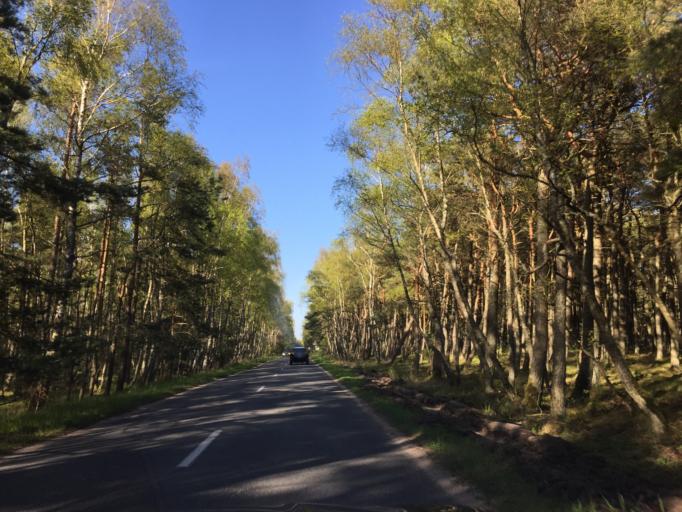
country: LT
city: Nida
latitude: 55.2193
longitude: 20.8879
